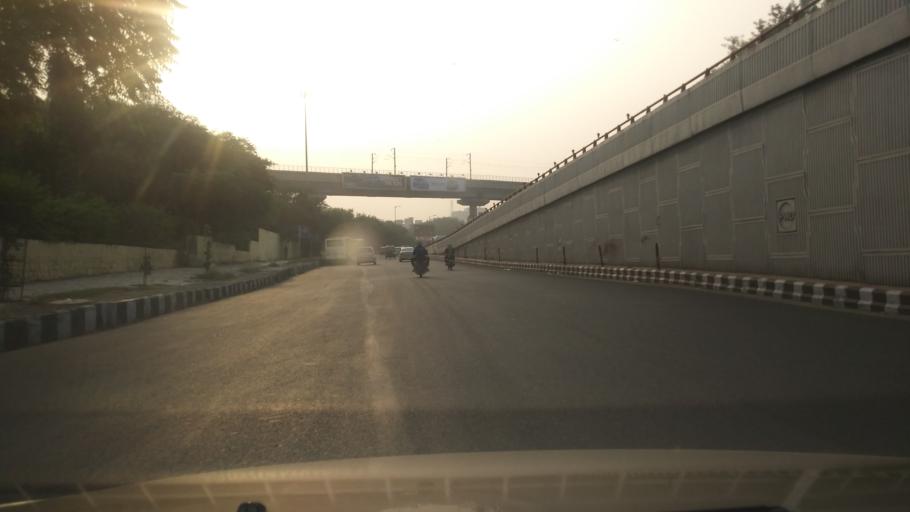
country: IN
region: Uttar Pradesh
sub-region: Gautam Buddha Nagar
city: Noida
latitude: 28.5492
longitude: 77.2617
